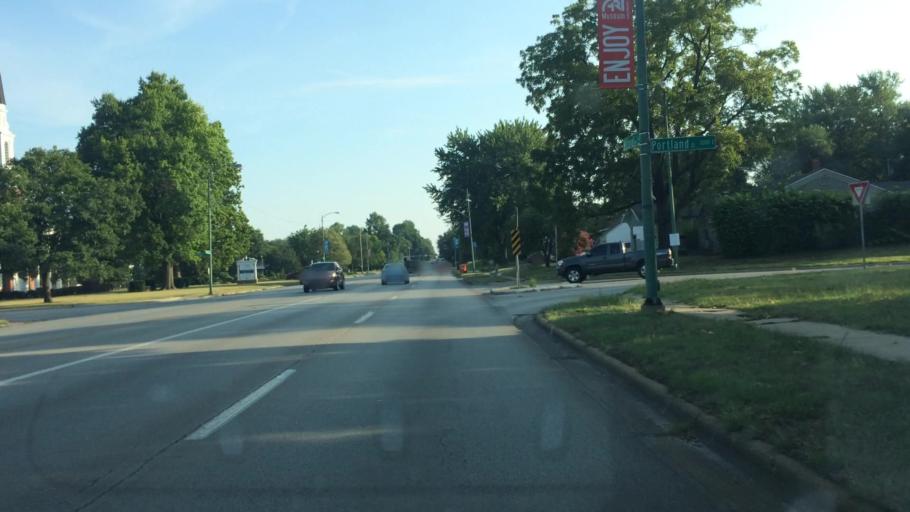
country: US
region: Missouri
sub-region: Greene County
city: Springfield
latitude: 37.1853
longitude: -93.2765
